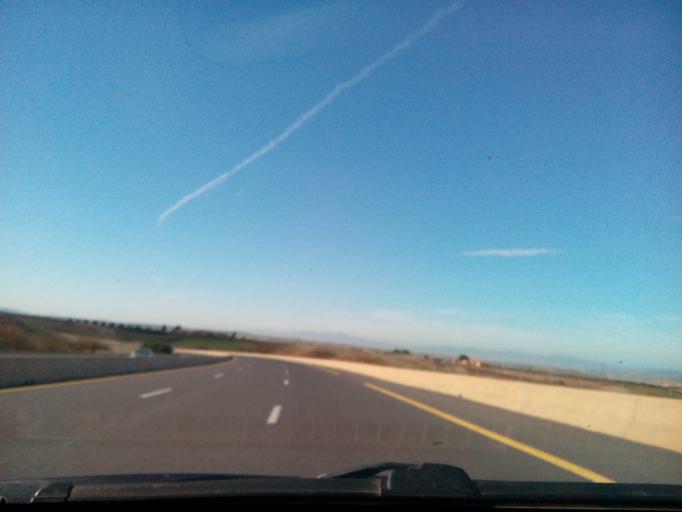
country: DZ
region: Tlemcen
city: Sidi Abdelli
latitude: 35.0098
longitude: -1.1774
